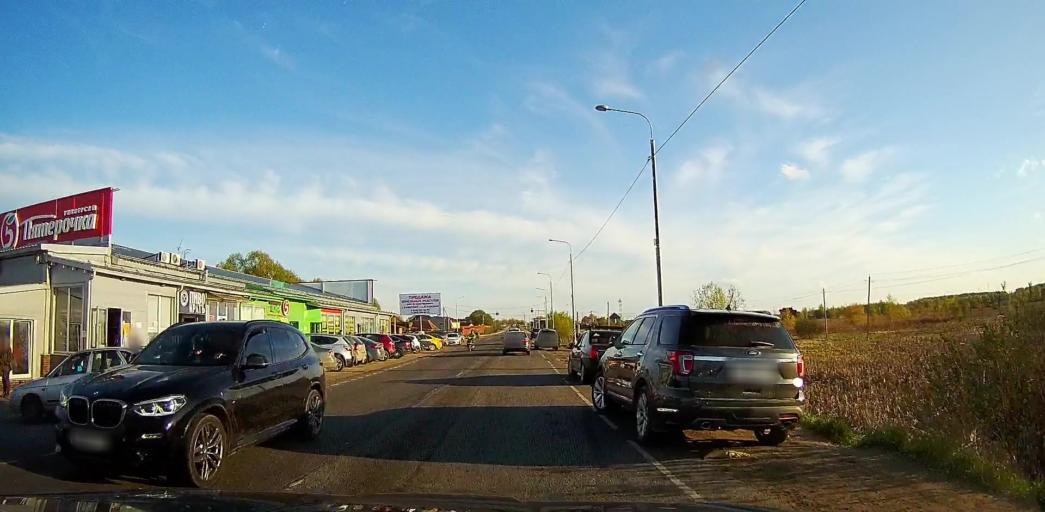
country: RU
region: Moskovskaya
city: Bronnitsy
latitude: 55.3300
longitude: 38.2195
